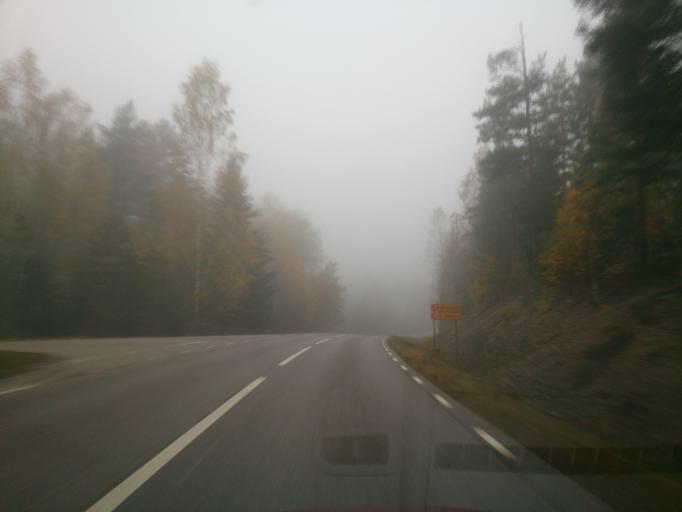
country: SE
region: OEstergoetland
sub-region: Atvidabergs Kommun
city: Atvidaberg
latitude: 58.0811
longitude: 15.9273
